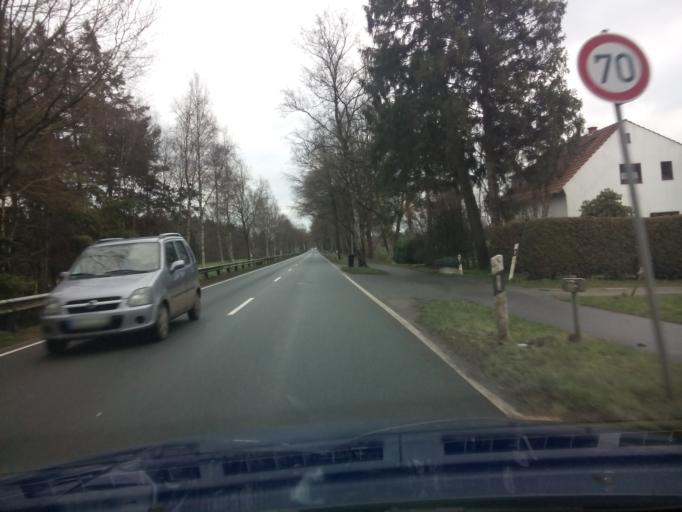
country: DE
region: Lower Saxony
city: Worpswede
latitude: 53.1989
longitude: 8.9360
